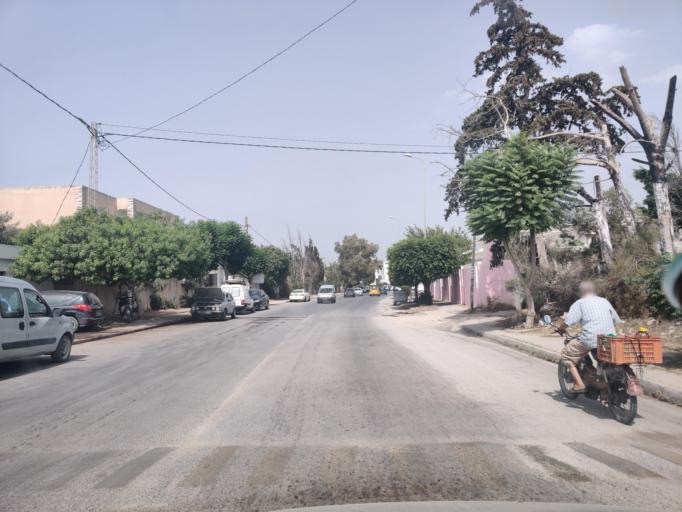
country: TN
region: Nabul
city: Al Hammamat
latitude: 36.4096
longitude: 10.6030
